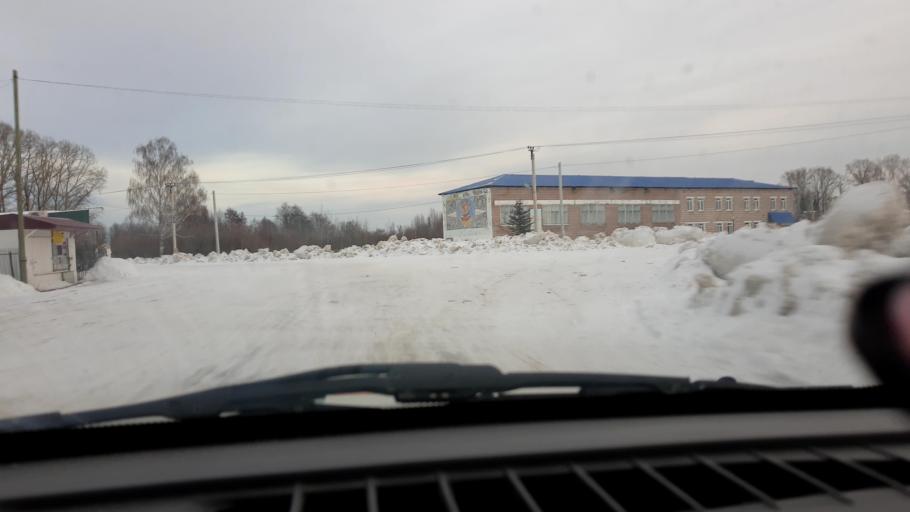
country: RU
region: Bashkortostan
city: Urman
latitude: 54.8651
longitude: 56.8532
